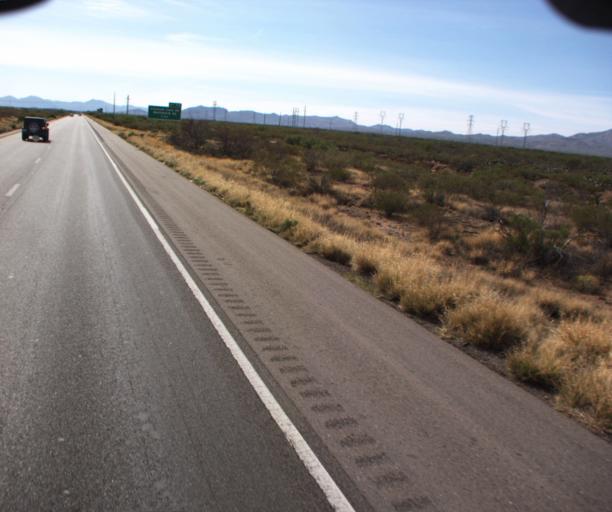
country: US
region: Arizona
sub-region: Pima County
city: Vail
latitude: 32.0389
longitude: -110.7384
